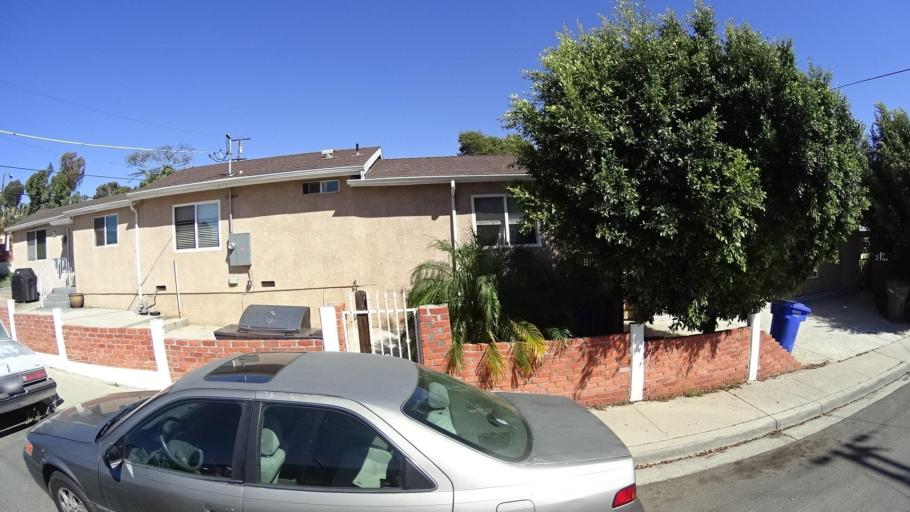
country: US
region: California
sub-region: San Diego County
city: Chula Vista
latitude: 32.6617
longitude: -117.0742
